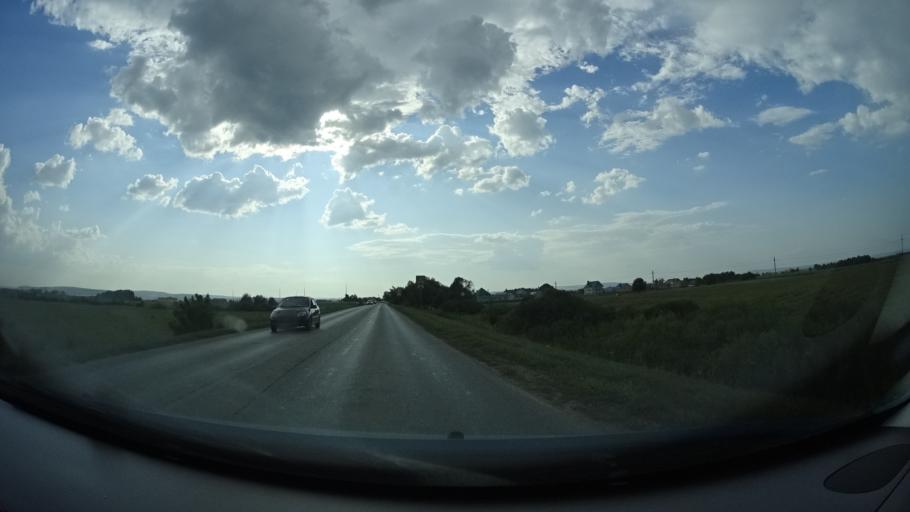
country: RU
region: Bashkortostan
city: Oktyabr'skiy
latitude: 54.4863
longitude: 53.4205
